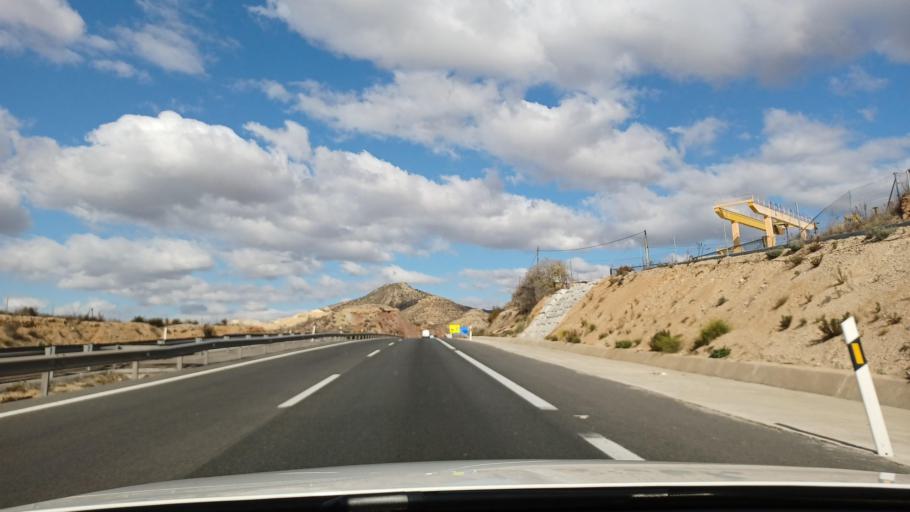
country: ES
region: Valencia
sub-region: Provincia de Alicante
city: Novelda
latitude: 38.4221
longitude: -0.7819
